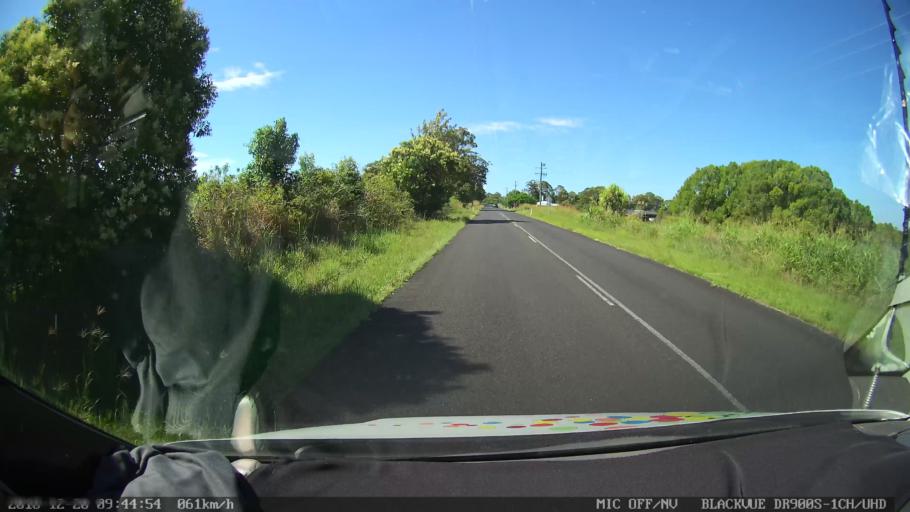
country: AU
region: New South Wales
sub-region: Lismore Municipality
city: Lismore
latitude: -28.7388
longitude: 153.2994
